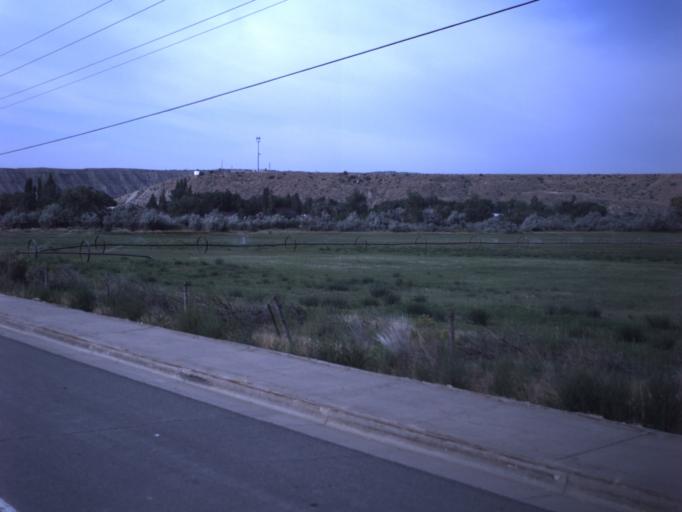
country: US
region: Utah
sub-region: Duchesne County
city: Duchesne
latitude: 40.1721
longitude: -110.4011
